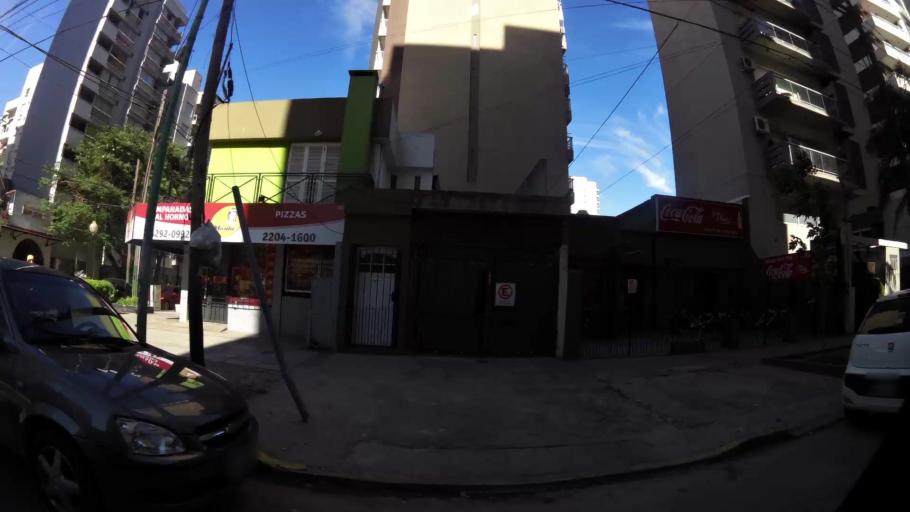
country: AR
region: Buenos Aires
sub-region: Partido de Lomas de Zamora
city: Lomas de Zamora
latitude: -34.7640
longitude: -58.4049
